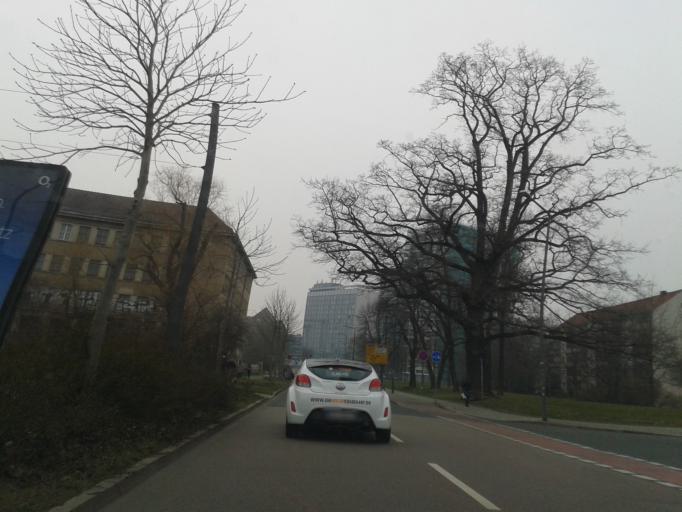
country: DE
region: Saxony
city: Dresden
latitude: 51.0393
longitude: 13.7387
